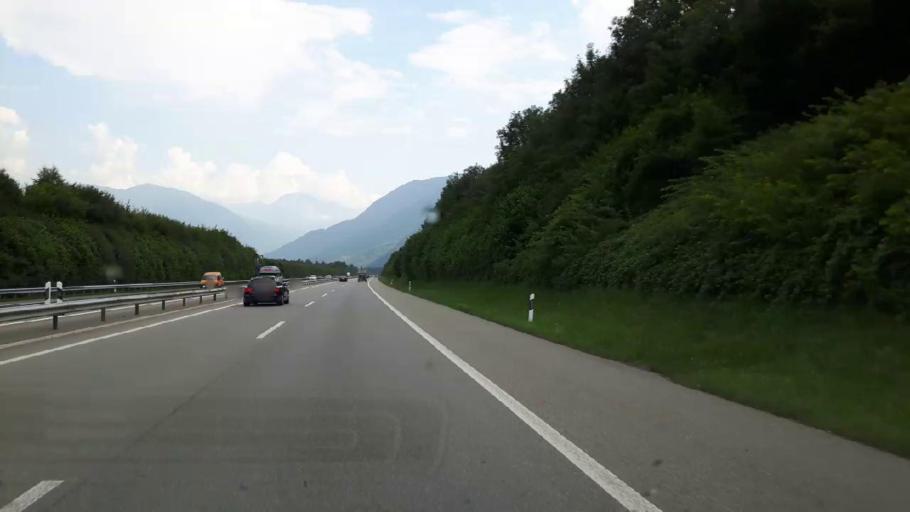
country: CH
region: Ticino
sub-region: Riviera District
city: Lodrino
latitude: 46.2958
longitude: 8.9893
